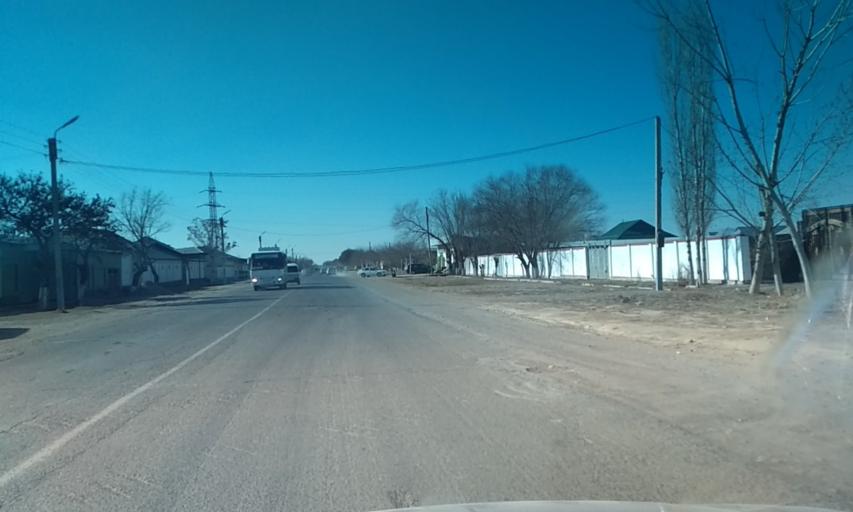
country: UZ
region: Sirdaryo
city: Guliston
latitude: 40.4936
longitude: 68.8111
